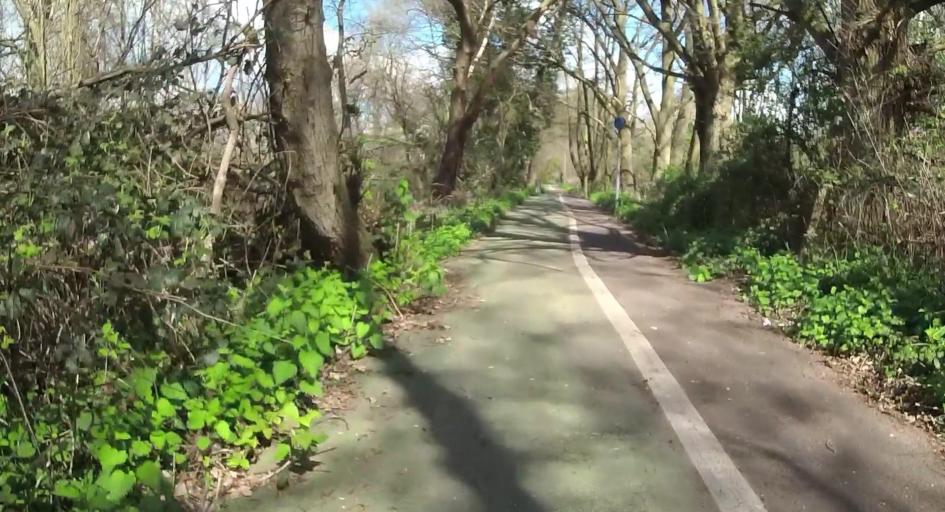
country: GB
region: England
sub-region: Surrey
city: Chertsey
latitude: 51.3806
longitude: -0.5034
